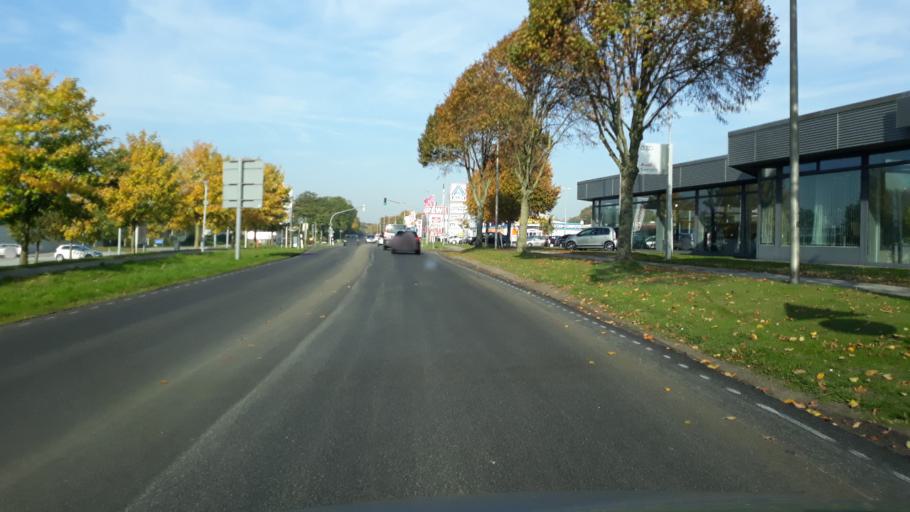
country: DE
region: Schleswig-Holstein
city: Schleswig
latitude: 54.5312
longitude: 9.5740
